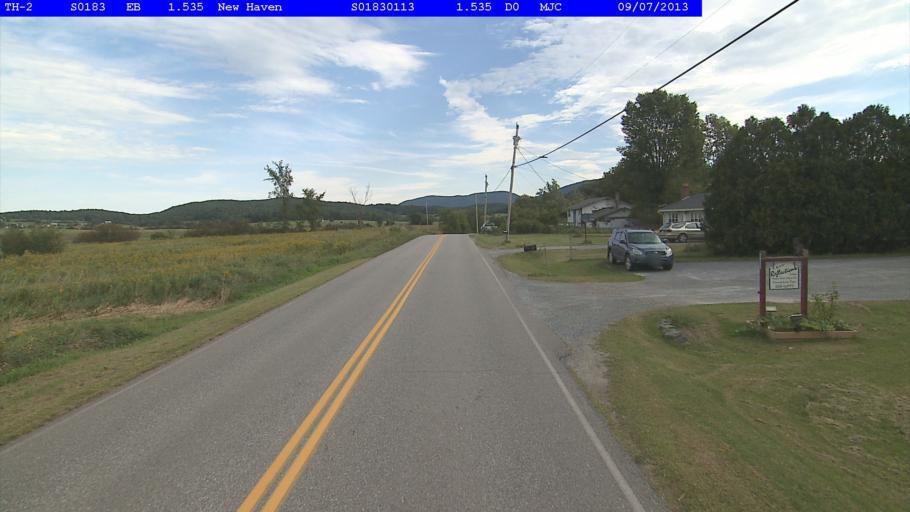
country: US
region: Vermont
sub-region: Addison County
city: Middlebury (village)
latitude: 44.0666
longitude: -73.1441
